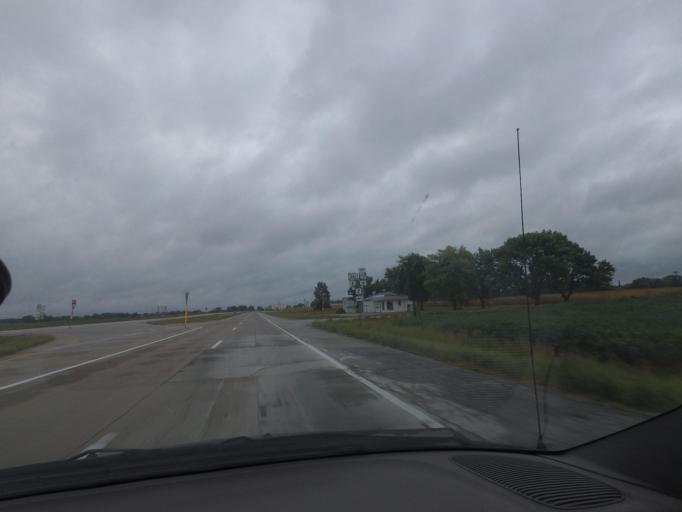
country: US
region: Missouri
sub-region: Marion County
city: Monroe City
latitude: 39.6734
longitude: -91.8661
